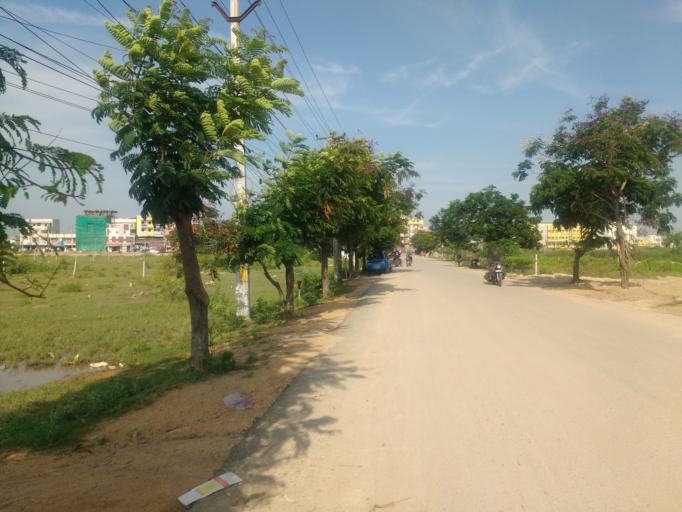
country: IN
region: Telangana
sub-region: Medak
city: Patancheru
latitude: 17.5315
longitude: 78.3006
